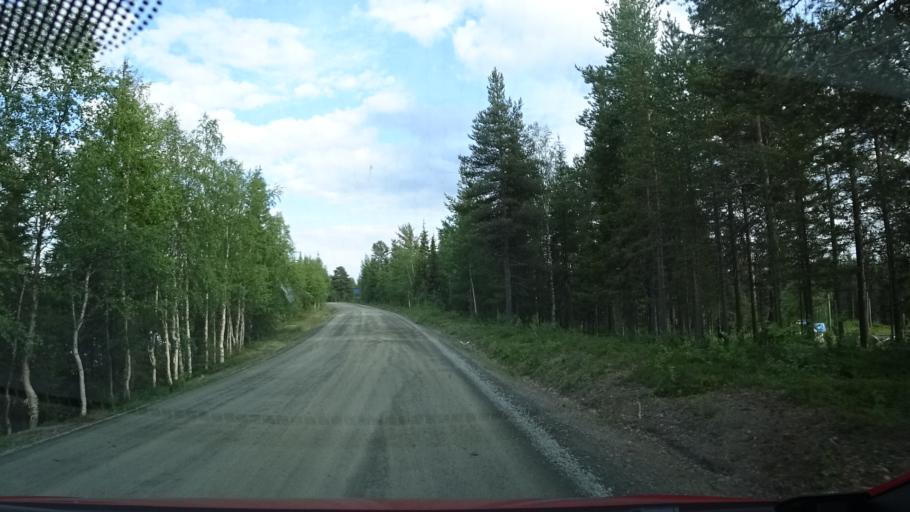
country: FI
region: Lapland
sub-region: Tunturi-Lappi
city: Kittilae
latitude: 67.9059
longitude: 25.0811
